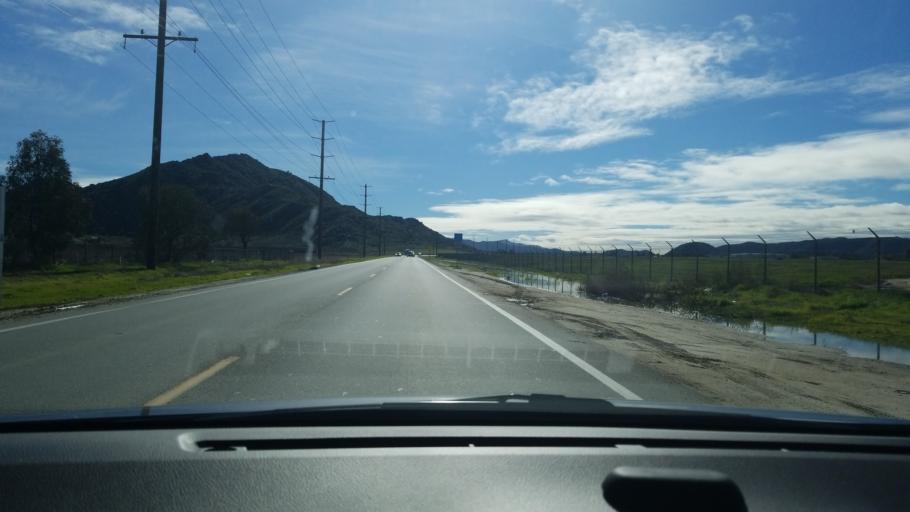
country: US
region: California
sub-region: Riverside County
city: Green Acres
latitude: 33.7720
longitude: -117.0334
